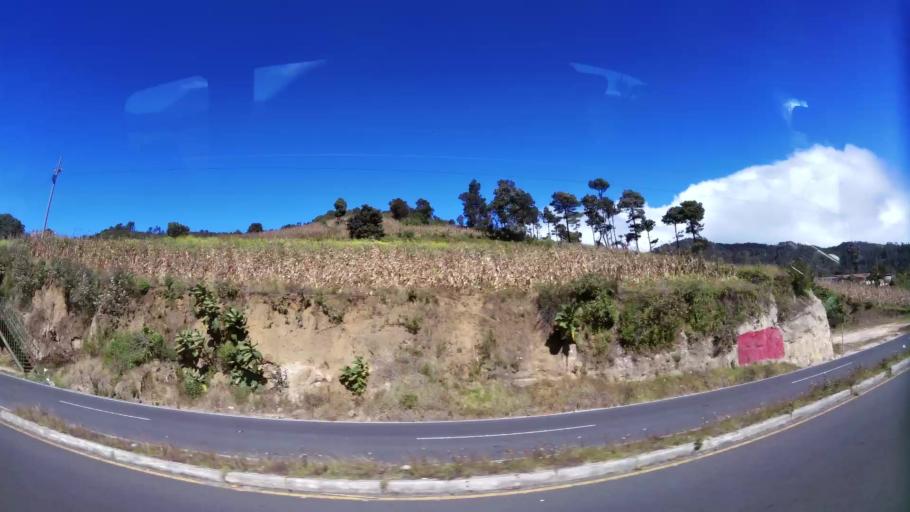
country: GT
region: Solola
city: Solola
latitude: 14.8213
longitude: -91.1997
